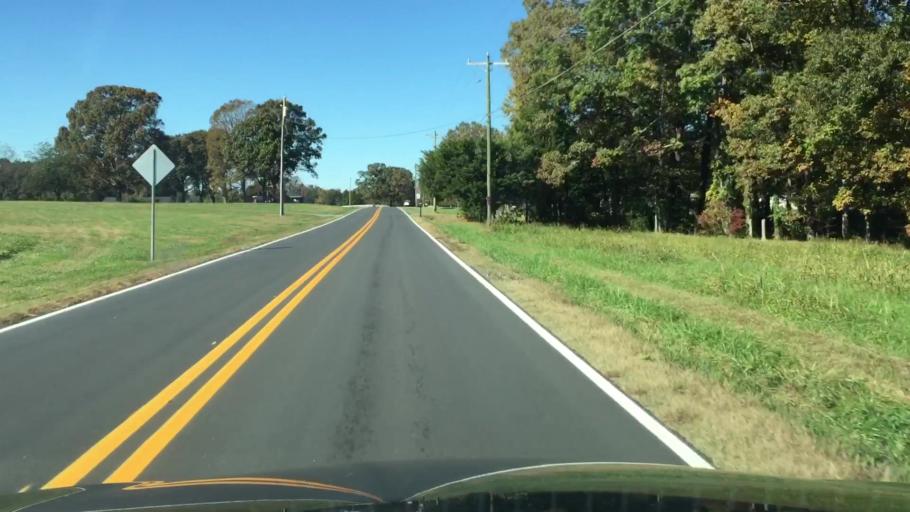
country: US
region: North Carolina
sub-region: Iredell County
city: Mooresville
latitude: 35.5691
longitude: -80.7763
